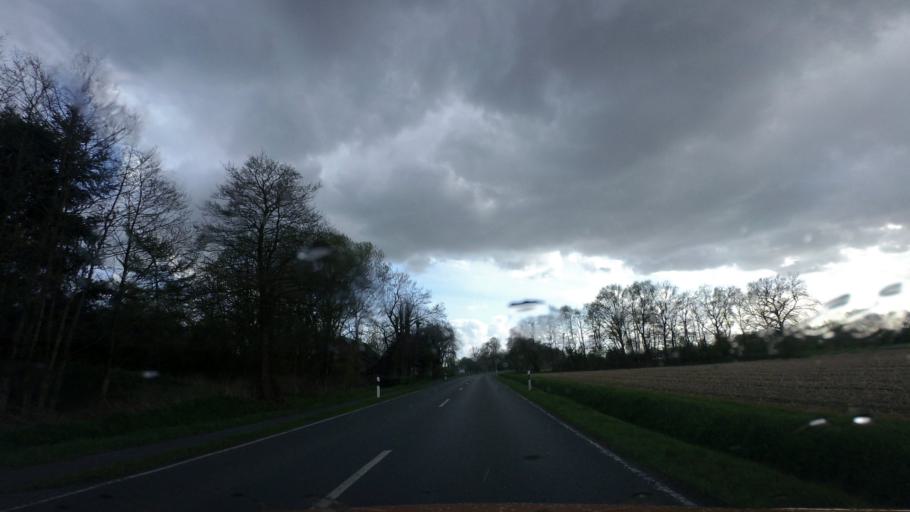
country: DE
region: Lower Saxony
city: Hude
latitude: 53.1089
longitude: 8.4374
